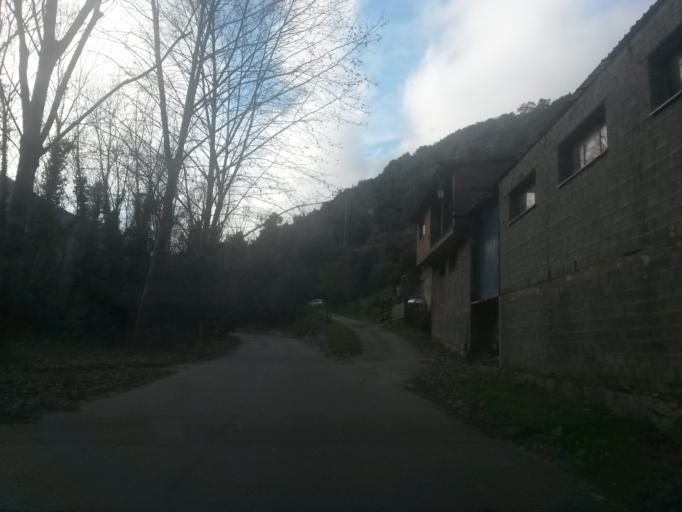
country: ES
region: Catalonia
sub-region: Provincia de Girona
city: Susqueda
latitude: 41.9866
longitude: 2.5478
